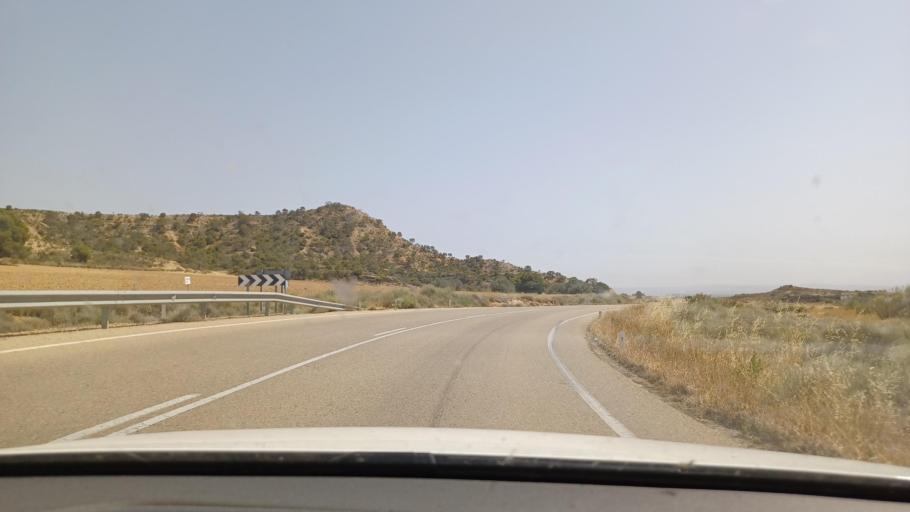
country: ES
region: Aragon
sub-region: Provincia de Zaragoza
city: Chiprana
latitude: 41.3368
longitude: -0.0888
